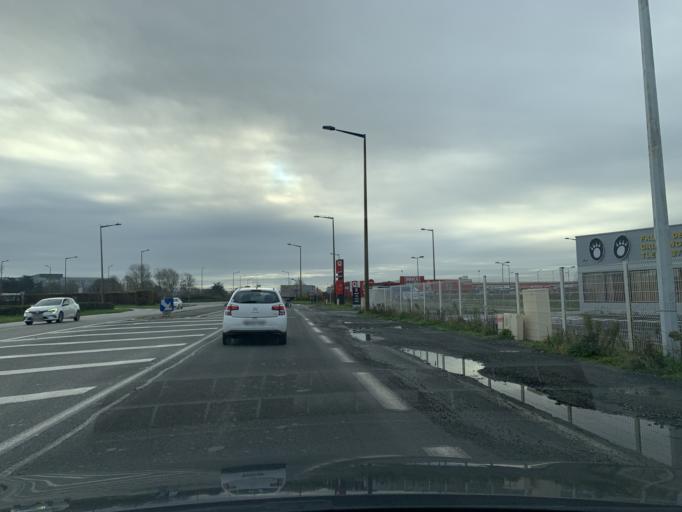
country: FR
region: Nord-Pas-de-Calais
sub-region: Departement du Nord
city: Dechy
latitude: 50.3408
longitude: 3.0961
